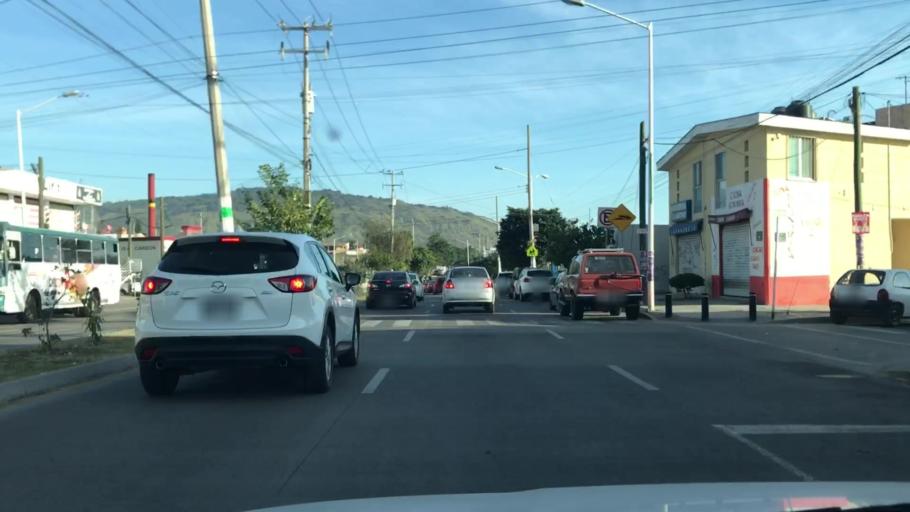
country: MX
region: Jalisco
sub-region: Tlajomulco de Zuniga
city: Palomar
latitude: 20.6281
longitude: -103.4607
